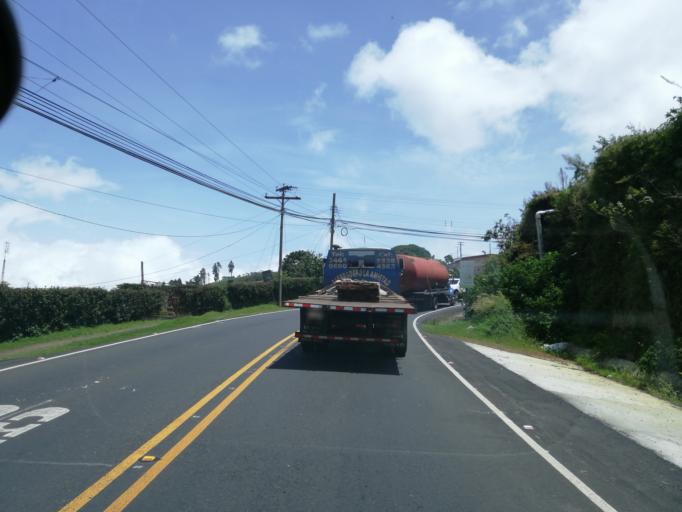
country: CR
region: Alajuela
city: Zarcero
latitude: 10.2160
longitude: -84.3998
